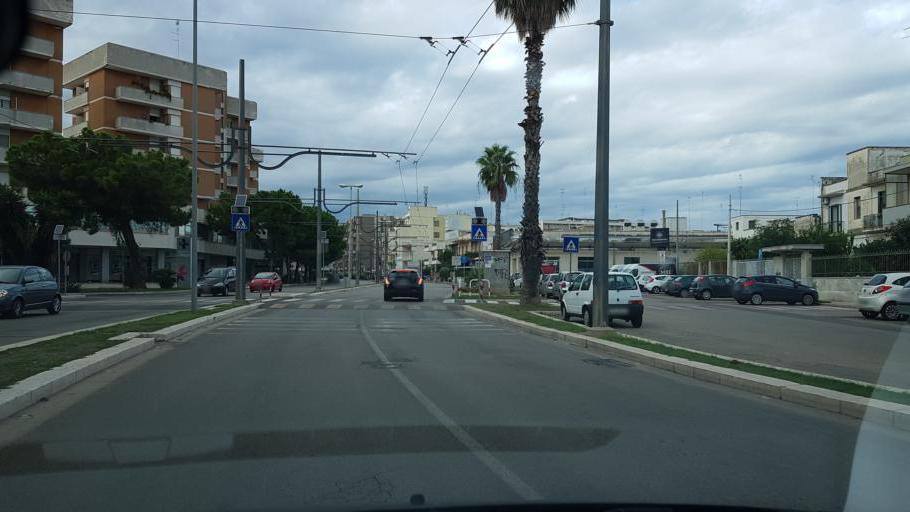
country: IT
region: Apulia
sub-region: Provincia di Lecce
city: Lecce
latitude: 40.3593
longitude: 18.1823
